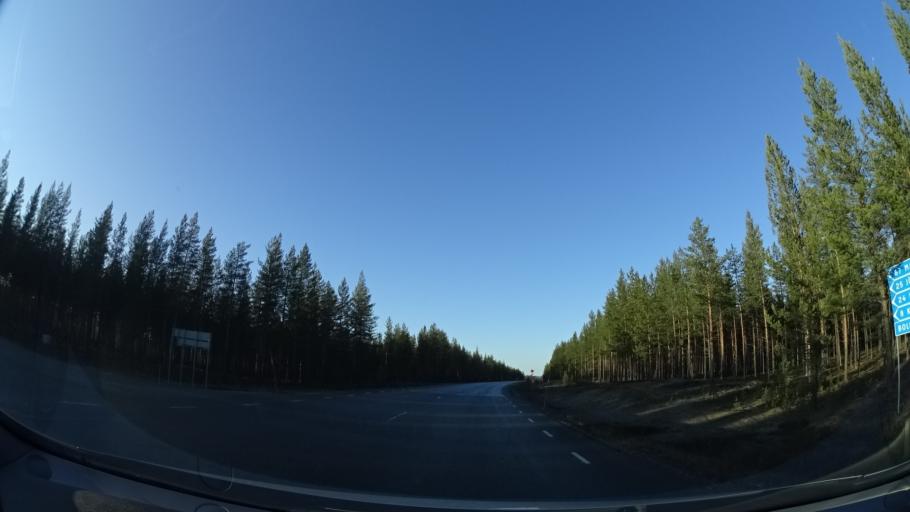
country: SE
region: Vaesterbotten
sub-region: Skelleftea Kommun
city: Langsele
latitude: 64.9484
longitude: 19.9129
